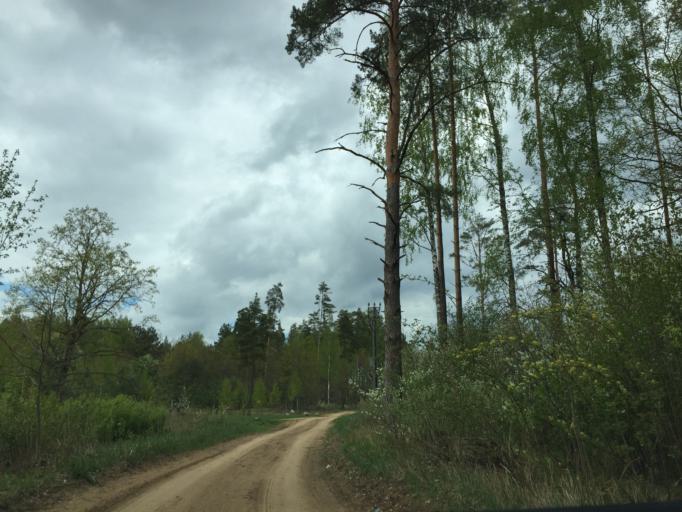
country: LV
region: Kekava
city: Kekava
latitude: 56.8019
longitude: 24.2994
